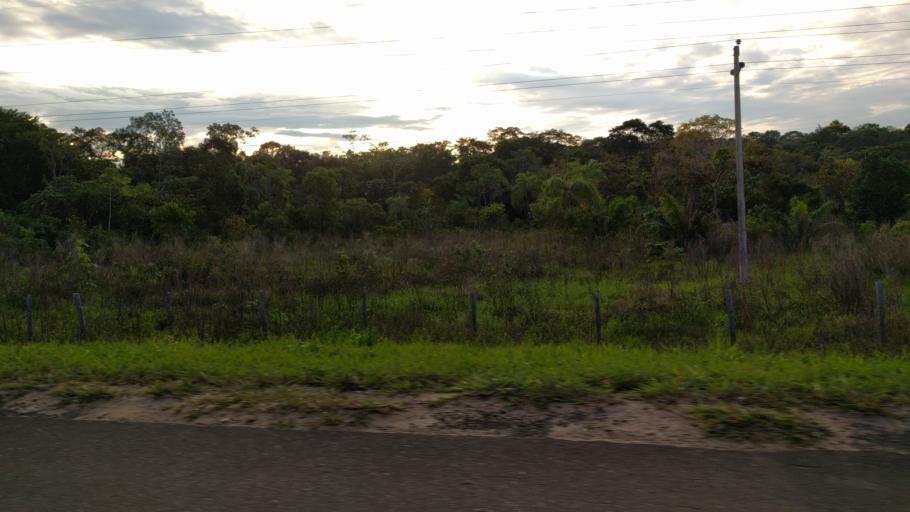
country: BO
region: Santa Cruz
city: Buena Vista
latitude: -17.4373
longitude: -63.6410
